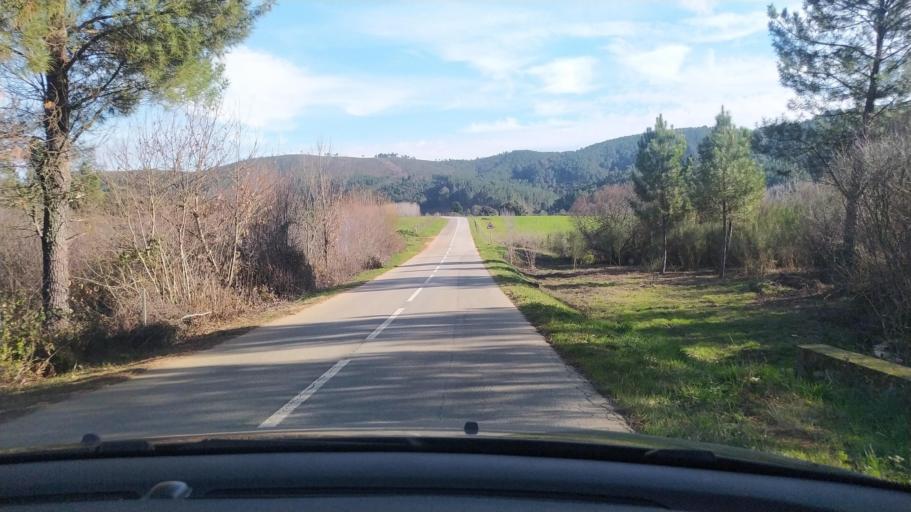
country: PT
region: Castelo Branco
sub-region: Concelho do Fundao
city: Aldeia de Joanes
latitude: 40.1800
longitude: -7.6588
